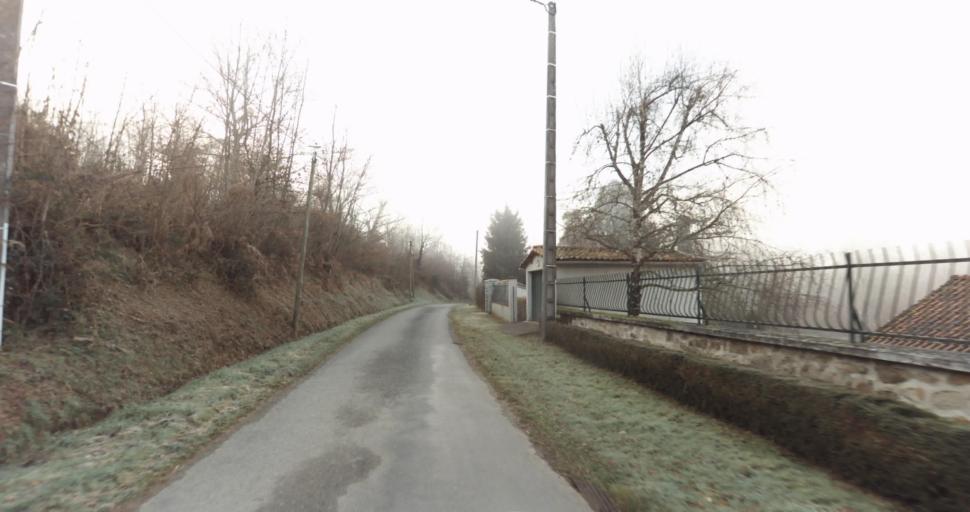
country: FR
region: Limousin
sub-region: Departement de la Haute-Vienne
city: Saint-Priest-sous-Aixe
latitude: 45.8187
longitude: 1.1195
